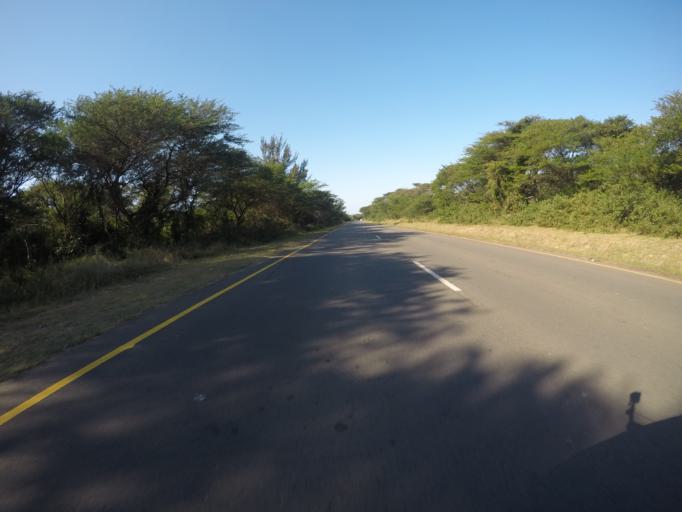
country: ZA
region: KwaZulu-Natal
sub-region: uThungulu District Municipality
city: Richards Bay
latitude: -28.7818
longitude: 32.0694
